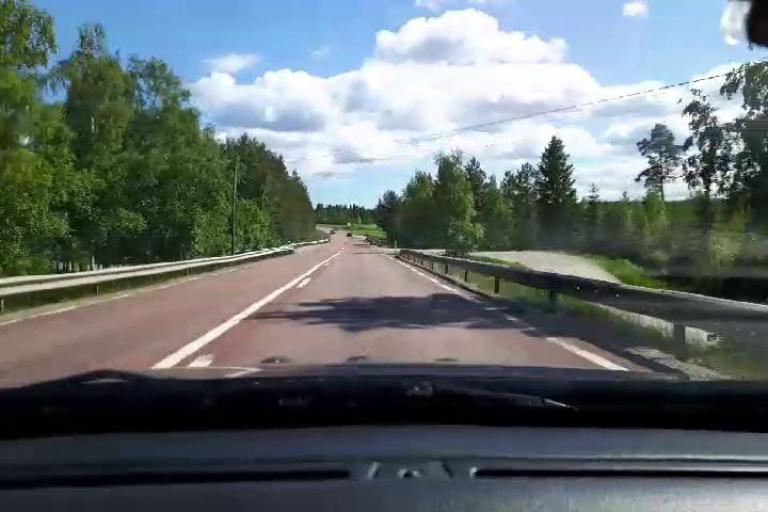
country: SE
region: Gaevleborg
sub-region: Hudiksvalls Kommun
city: Delsbo
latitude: 61.7841
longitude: 16.6346
